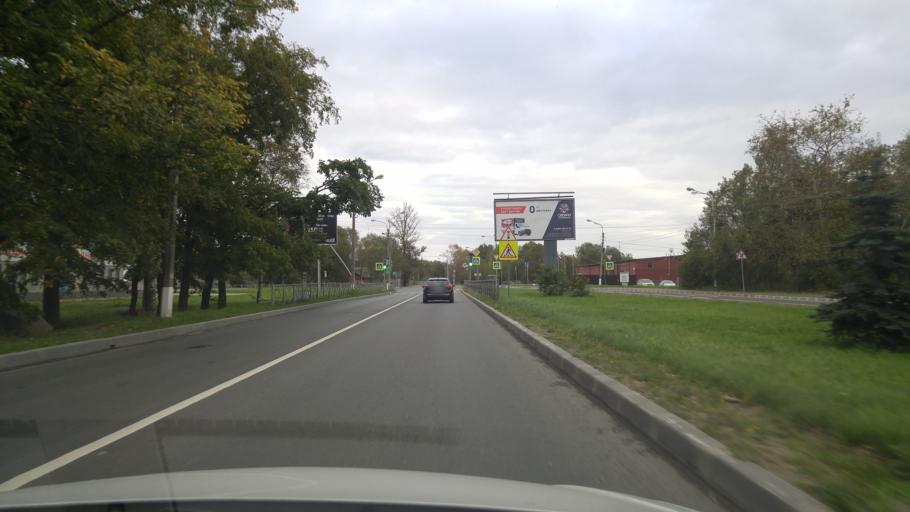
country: RU
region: St.-Petersburg
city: Kronshtadt
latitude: 60.0071
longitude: 29.7397
